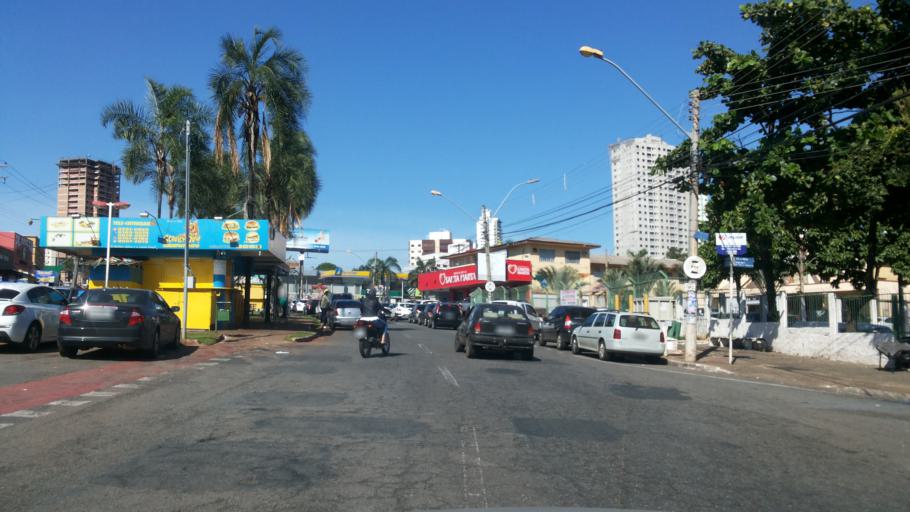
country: BR
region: Goias
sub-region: Goiania
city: Goiania
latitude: -16.7130
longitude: -49.2546
